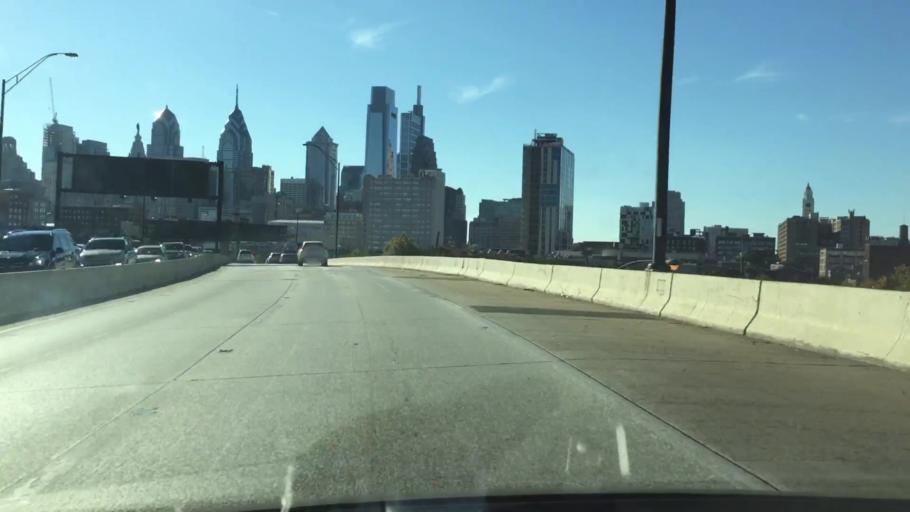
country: US
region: Pennsylvania
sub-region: Philadelphia County
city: Philadelphia
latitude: 39.9577
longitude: -75.1502
